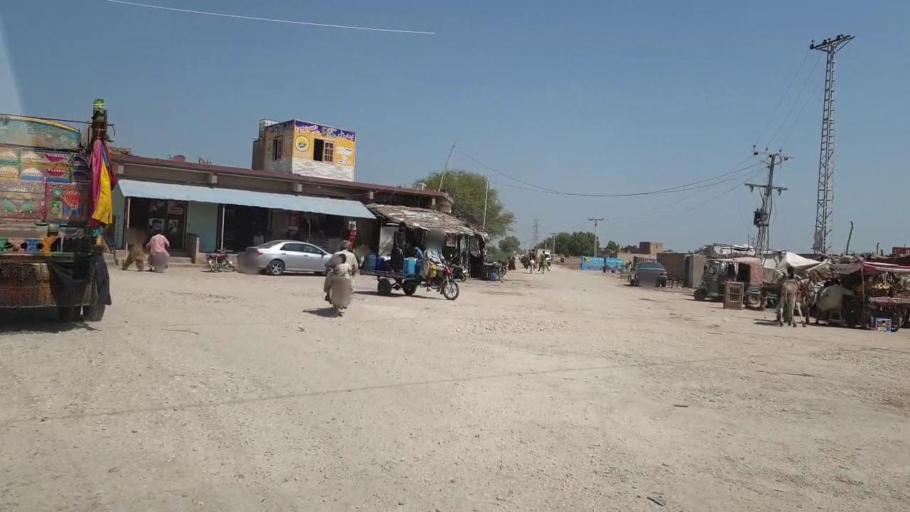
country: PK
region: Sindh
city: Hyderabad
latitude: 25.4306
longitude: 68.3972
